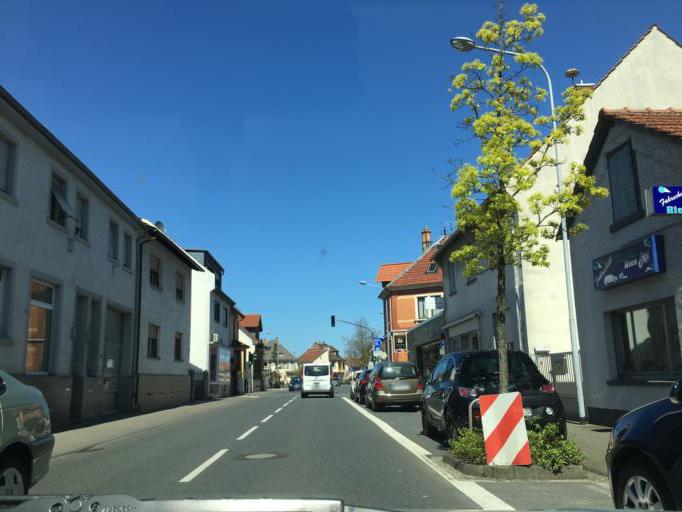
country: DE
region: Hesse
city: Obertshausen
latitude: 50.0810
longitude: 8.8648
